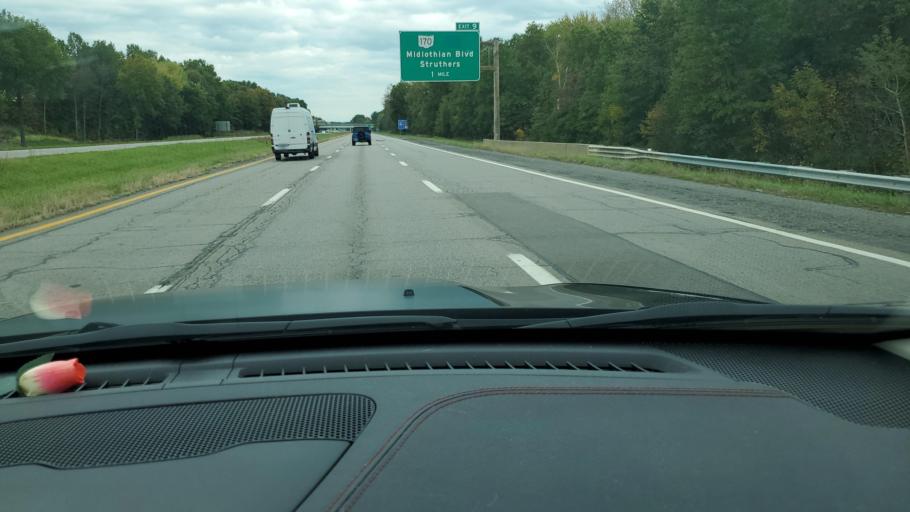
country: US
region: Ohio
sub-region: Mahoning County
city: Poland
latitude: 41.0423
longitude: -80.6308
